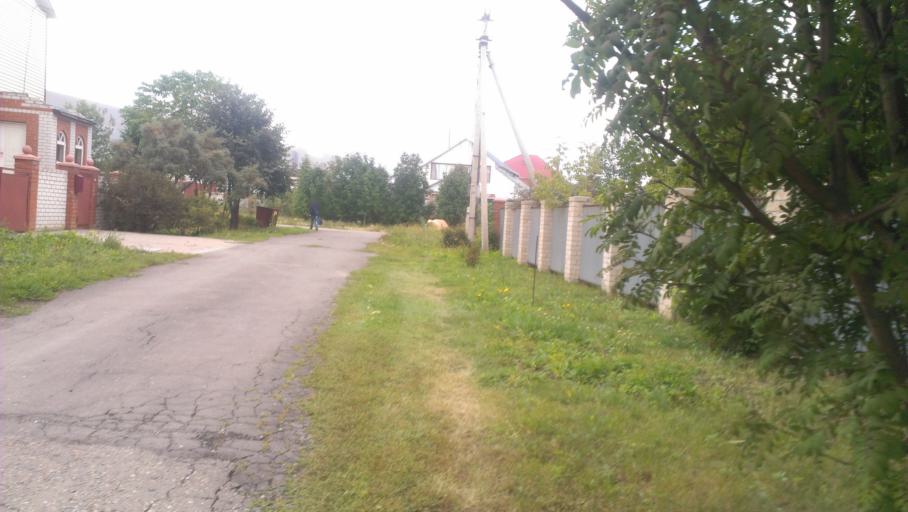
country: RU
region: Altai Krai
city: Novosilikatnyy
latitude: 53.3499
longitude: 83.6419
